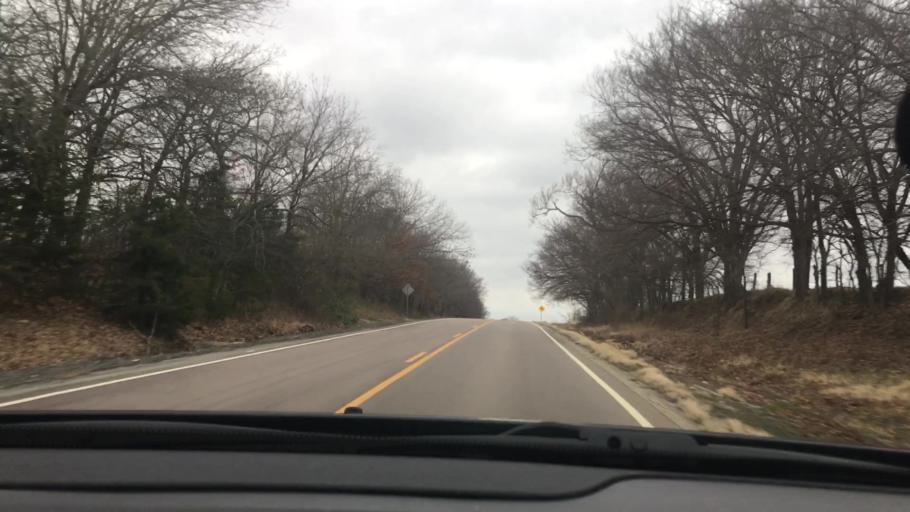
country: US
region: Oklahoma
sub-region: Coal County
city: Coalgate
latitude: 34.3727
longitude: -96.3565
